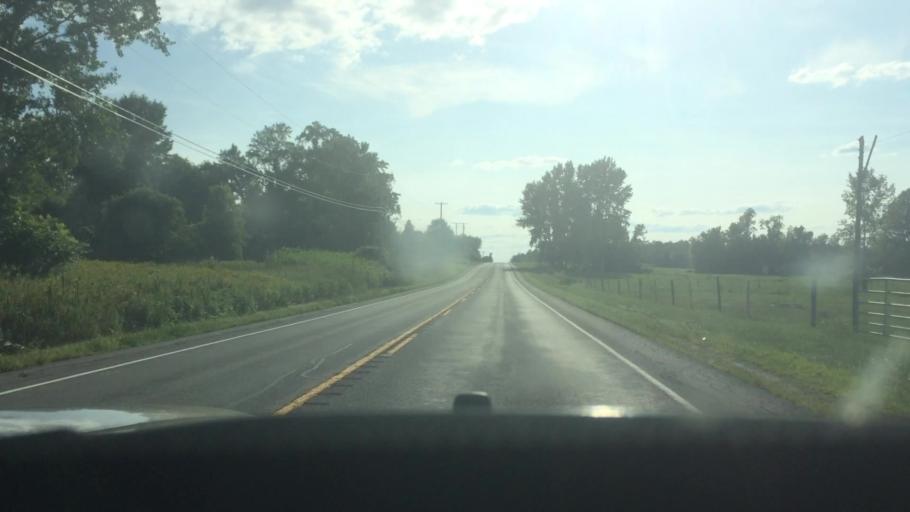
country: US
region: New York
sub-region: St. Lawrence County
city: Potsdam
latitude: 44.6822
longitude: -74.8169
